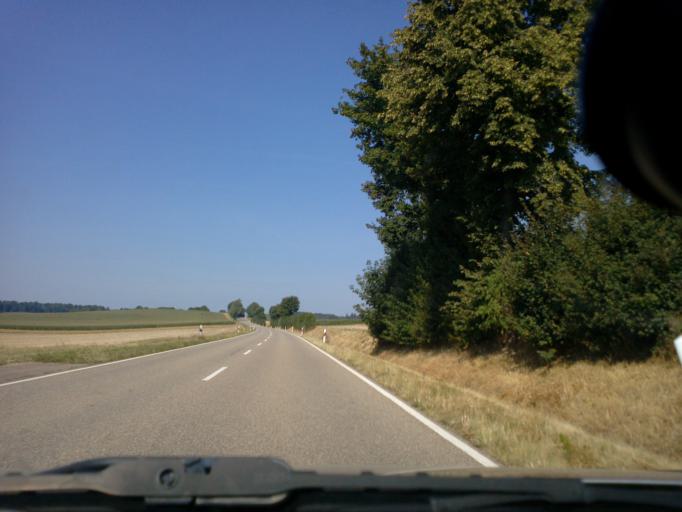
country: DE
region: Baden-Wuerttemberg
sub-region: Karlsruhe Region
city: Gondelsheim
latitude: 49.0604
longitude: 8.6391
